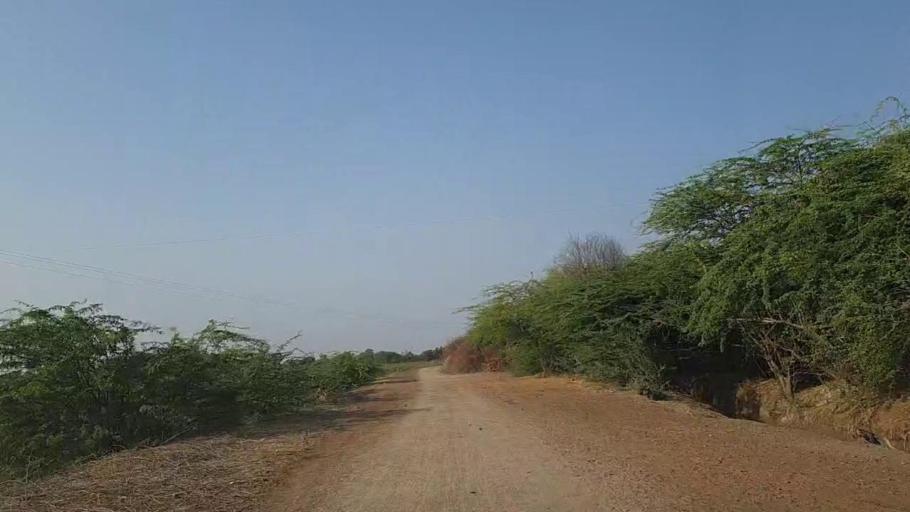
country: PK
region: Sindh
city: Dhoro Naro
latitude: 25.4925
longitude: 69.4994
